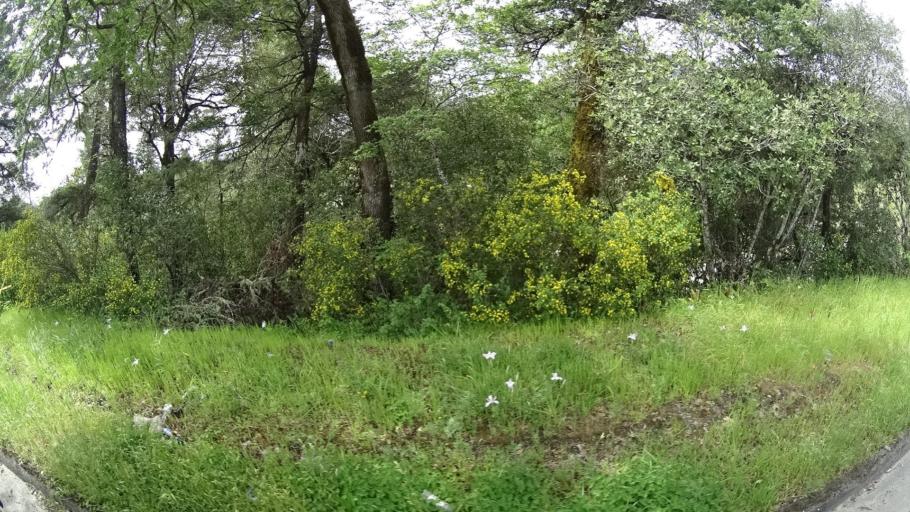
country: US
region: California
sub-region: Humboldt County
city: Redway
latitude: 40.1073
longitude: -123.7936
